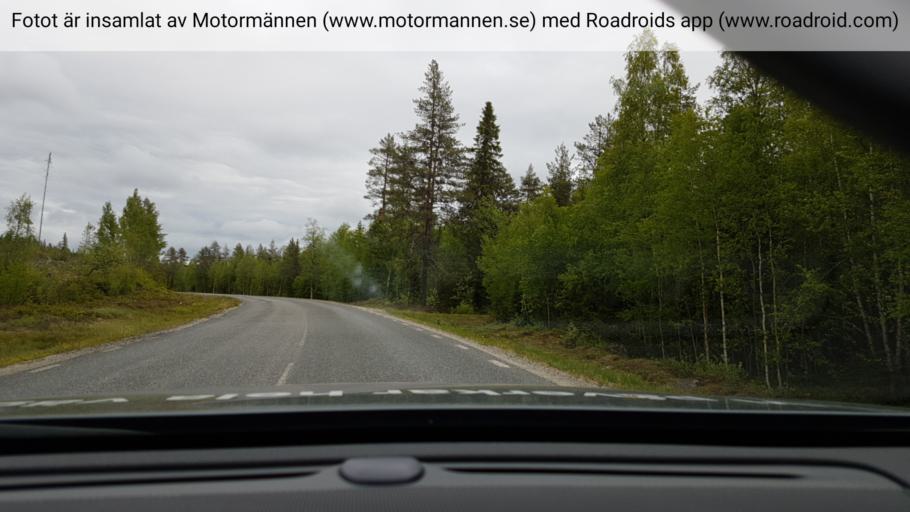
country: SE
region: Vaesterbotten
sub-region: Asele Kommun
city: Insjon
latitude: 64.3237
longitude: 17.7196
